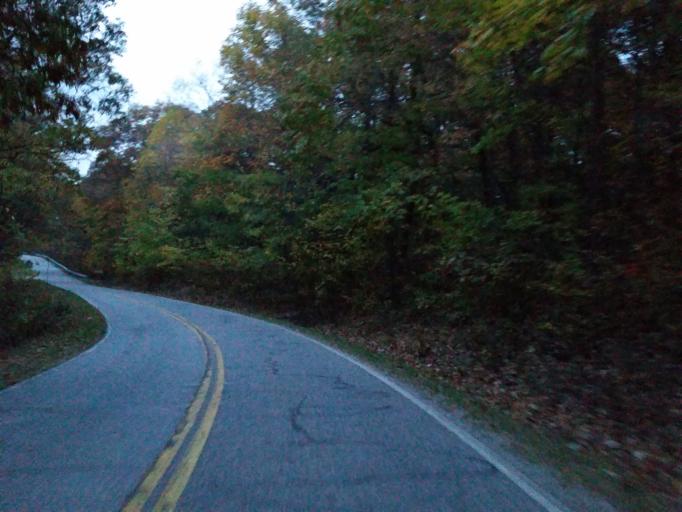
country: US
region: Georgia
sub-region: Lumpkin County
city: Dahlonega
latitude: 34.6643
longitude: -83.9827
